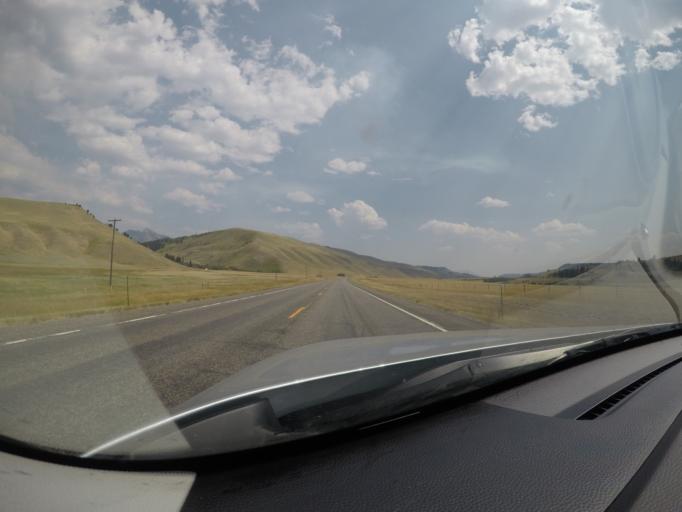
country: US
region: Montana
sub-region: Gallatin County
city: Big Sky
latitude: 44.9633
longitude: -111.6317
